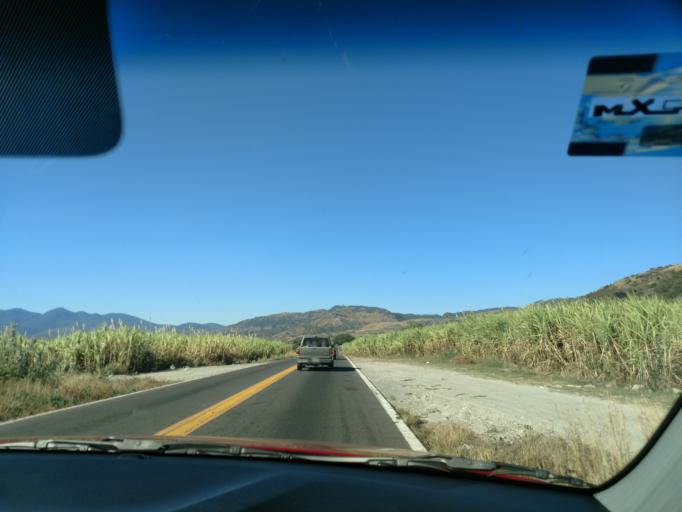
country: MX
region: Nayarit
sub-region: Ahuacatlan
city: Ahuacatlan
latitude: 21.1439
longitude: -104.6086
